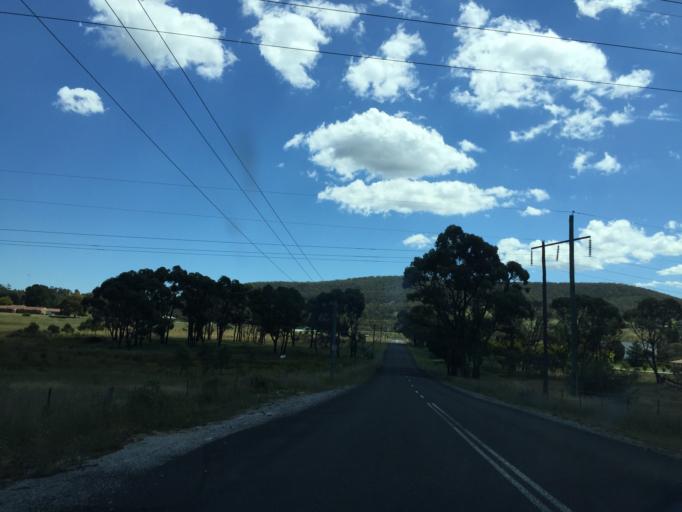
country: AU
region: New South Wales
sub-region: Lithgow
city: Lithgow
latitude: -33.4387
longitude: 150.1190
